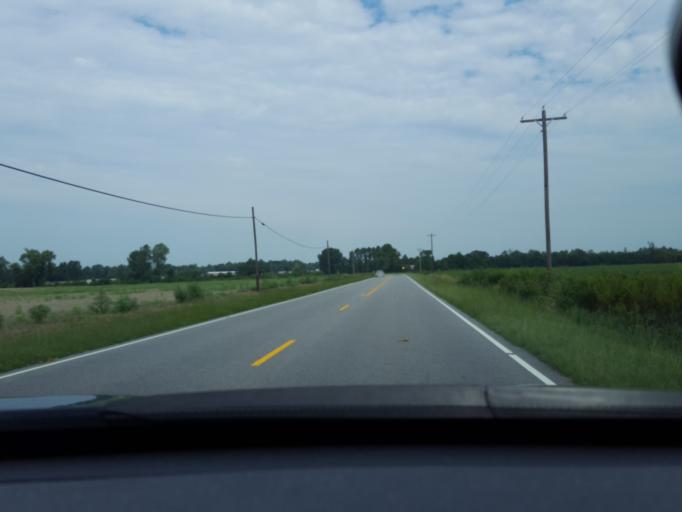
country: US
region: North Carolina
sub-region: Chowan County
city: Edenton
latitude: 36.1548
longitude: -76.6534
